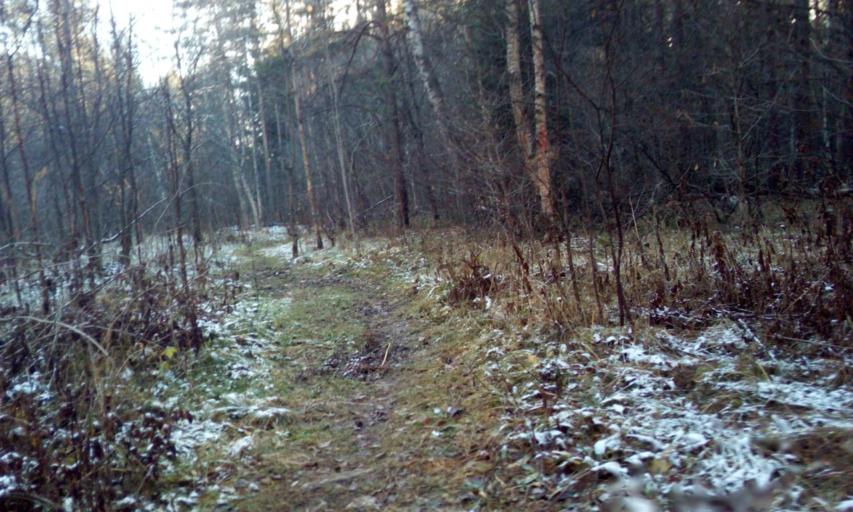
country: RU
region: Moskovskaya
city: Aprelevka
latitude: 55.5486
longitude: 37.0988
